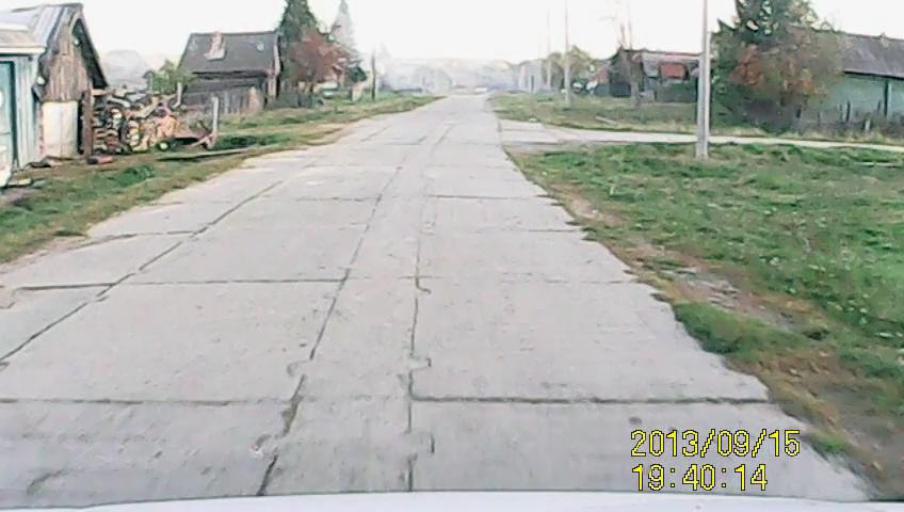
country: RU
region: Chelyabinsk
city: Kyshtym
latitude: 55.8488
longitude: 60.4815
